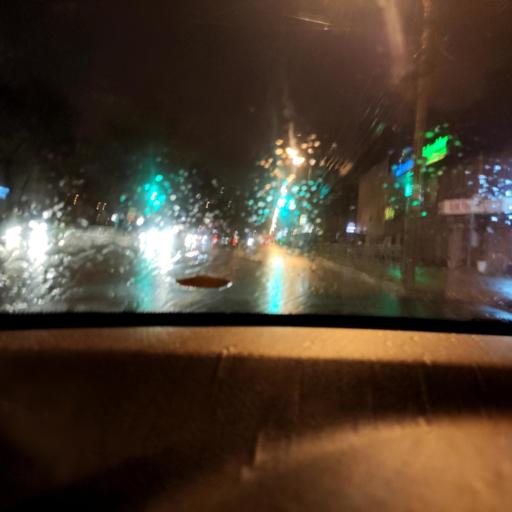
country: RU
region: Samara
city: Samara
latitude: 53.2106
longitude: 50.1893
